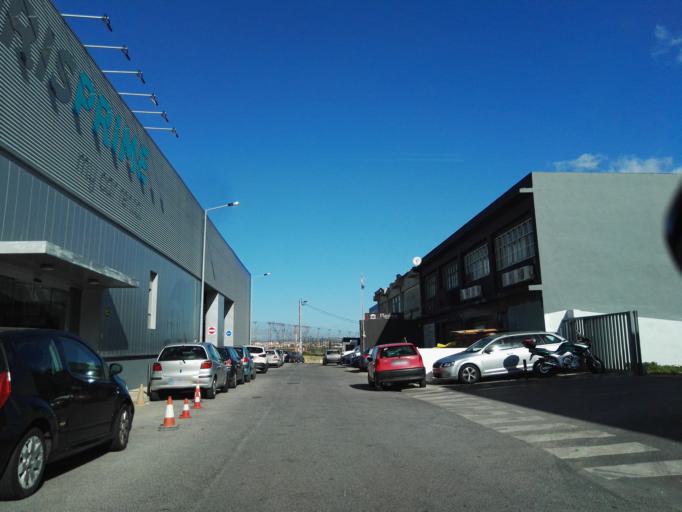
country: PT
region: Lisbon
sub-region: Loures
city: Camarate
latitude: 38.7863
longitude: -9.1308
